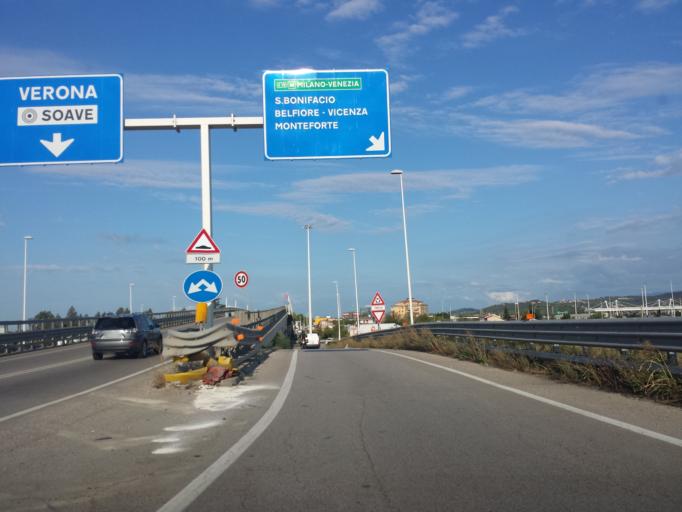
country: IT
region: Veneto
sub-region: Provincia di Verona
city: Soave
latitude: 45.4042
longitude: 11.2572
